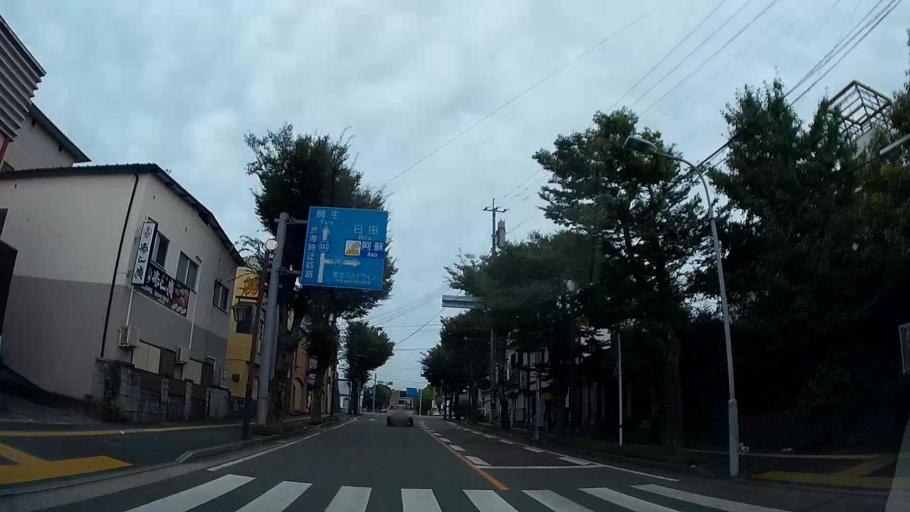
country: JP
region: Kumamoto
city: Kikuchi
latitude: 32.9838
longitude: 130.8147
